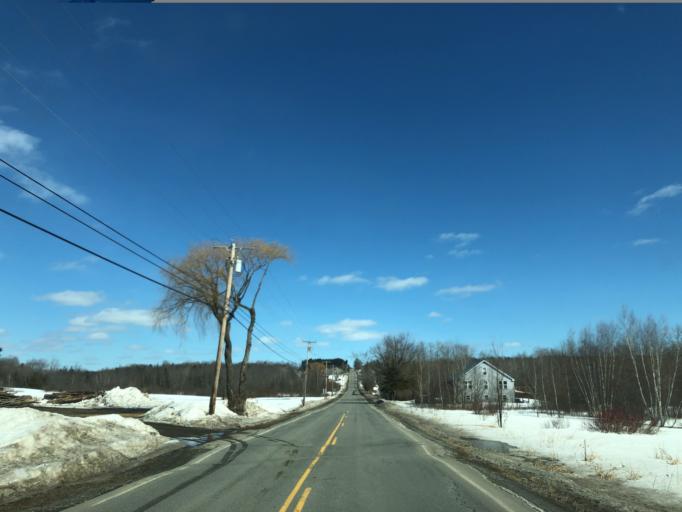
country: US
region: Maine
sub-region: Penobscot County
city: Corinna
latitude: 44.9241
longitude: -69.2525
